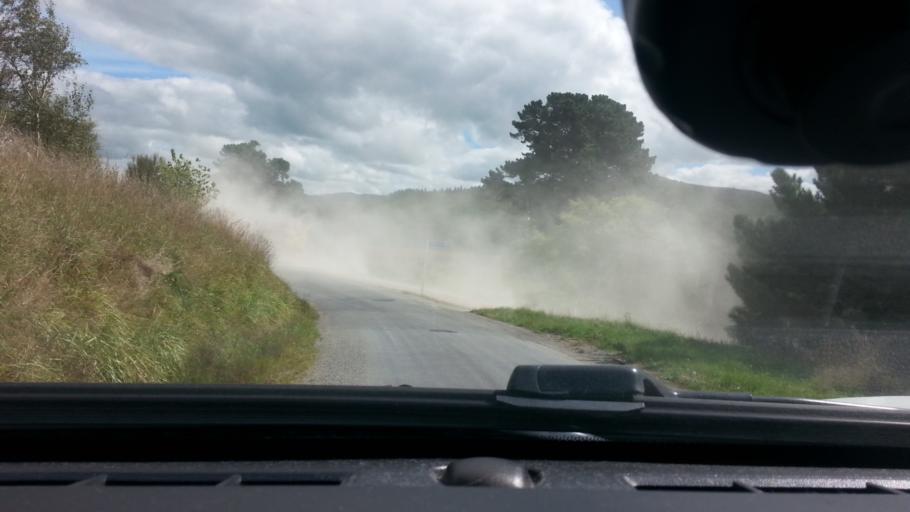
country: NZ
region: Wellington
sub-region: Masterton District
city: Masterton
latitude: -40.8433
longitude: 175.9033
